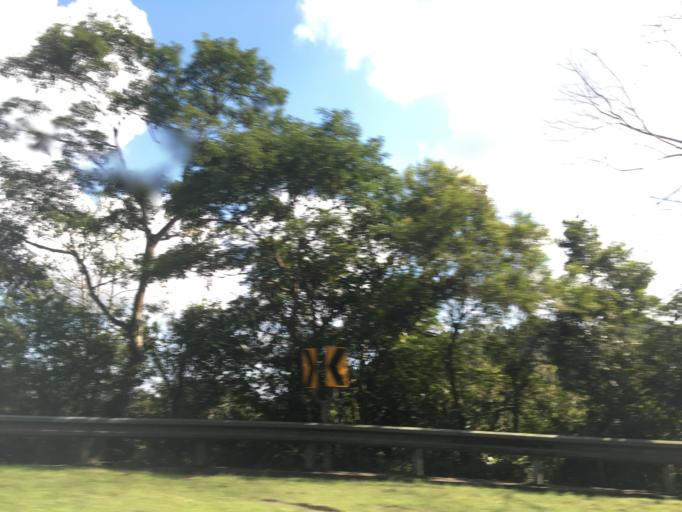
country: TW
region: Taiwan
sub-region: Yilan
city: Yilan
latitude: 24.7490
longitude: 121.6463
